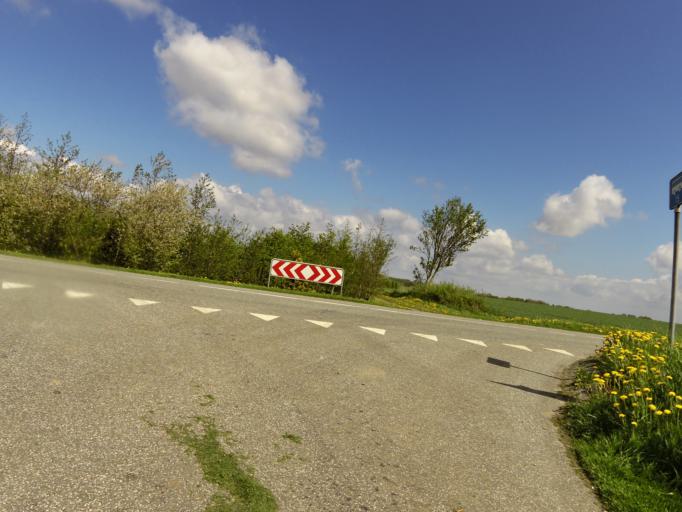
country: DK
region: South Denmark
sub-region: Haderslev Kommune
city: Gram
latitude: 55.3209
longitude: 9.0630
